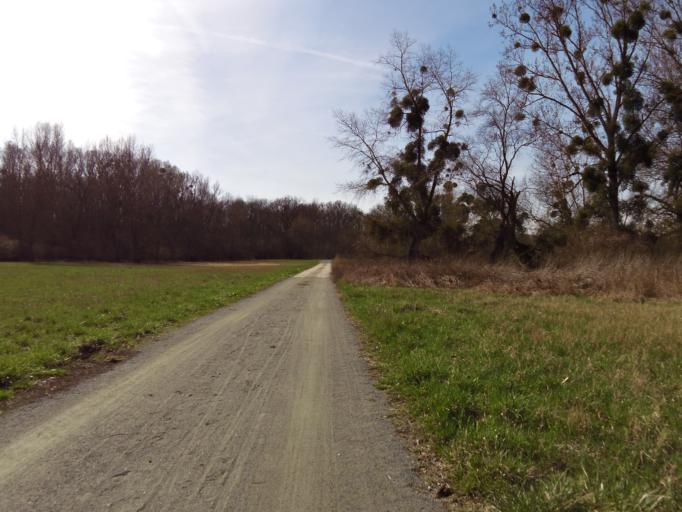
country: DE
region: Rheinland-Pfalz
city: Gimbsheim
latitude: 49.8070
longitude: 8.4165
